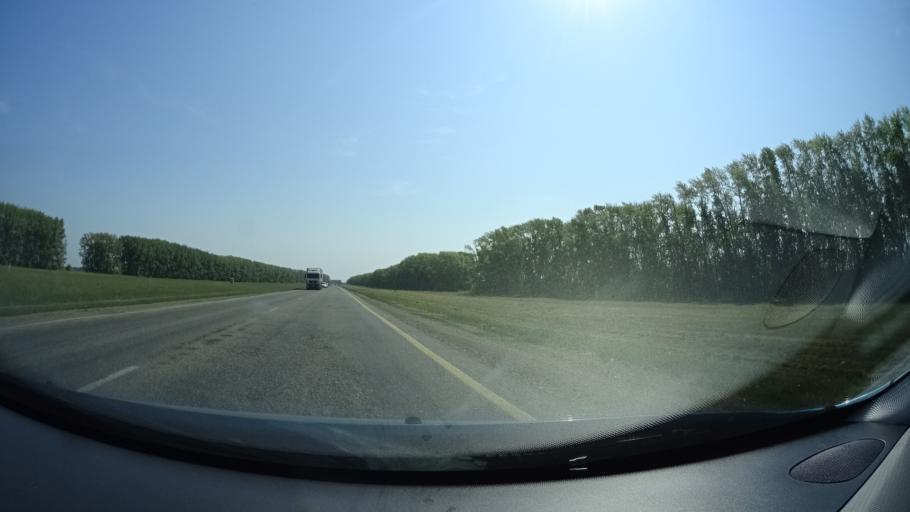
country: RU
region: Bashkortostan
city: Karmaskaly
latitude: 54.3947
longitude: 56.1109
